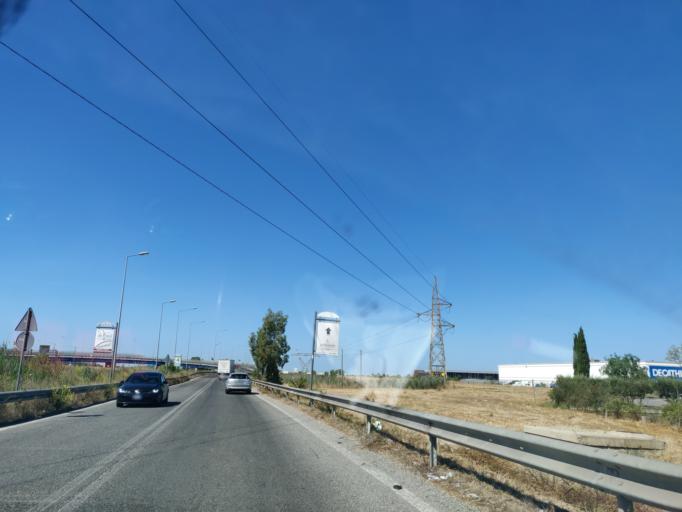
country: IT
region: Latium
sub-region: Citta metropolitana di Roma Capitale
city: Npp 23 (Parco Leonardo)
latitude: 41.8075
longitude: 12.3022
